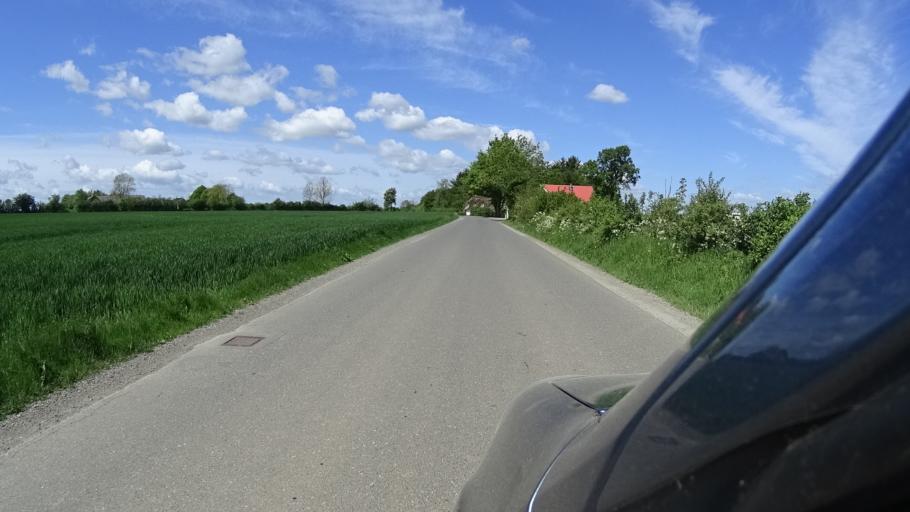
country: DK
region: South Denmark
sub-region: Vejle Kommune
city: Borkop
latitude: 55.6163
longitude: 9.6068
